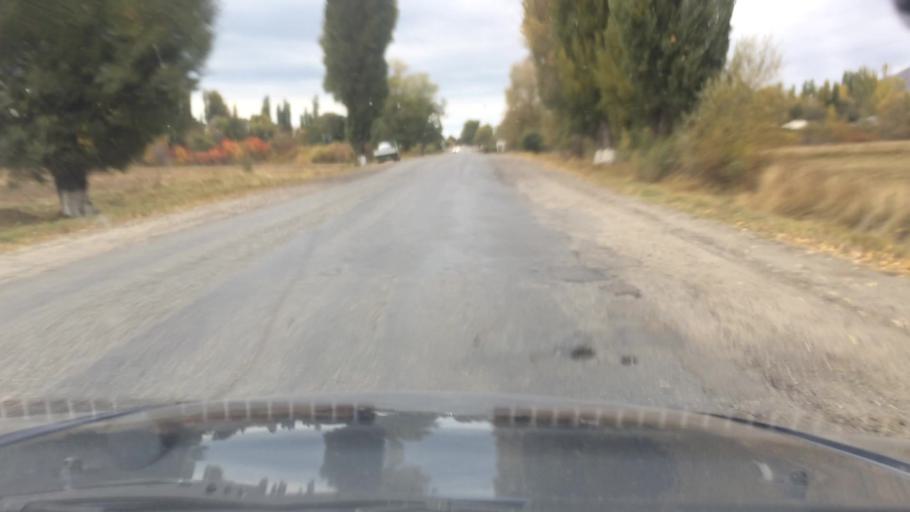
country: KG
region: Ysyk-Koel
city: Tyup
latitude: 42.7705
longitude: 78.1912
